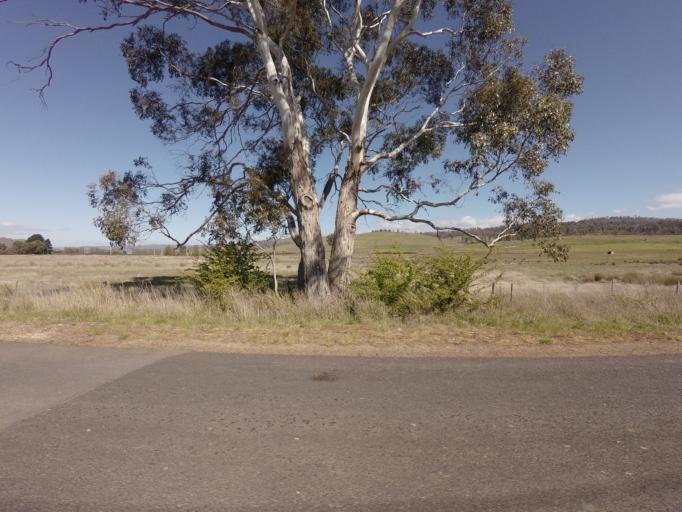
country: AU
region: Tasmania
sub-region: Derwent Valley
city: New Norfolk
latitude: -42.5367
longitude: 146.7283
